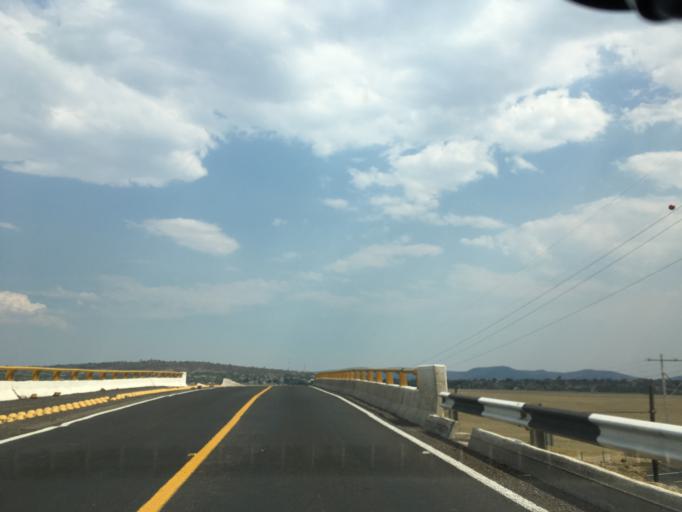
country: MX
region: Michoacan
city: Cuitzeo del Porvenir
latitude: 19.9878
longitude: -101.1491
